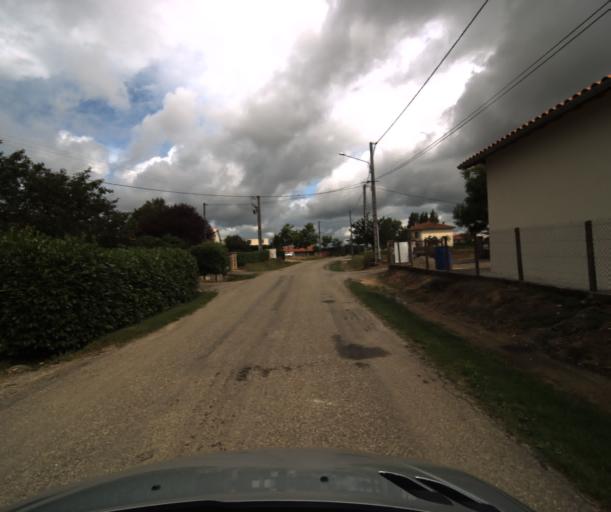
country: FR
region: Midi-Pyrenees
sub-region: Departement du Tarn-et-Garonne
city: Lavit
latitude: 43.9600
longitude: 0.9169
